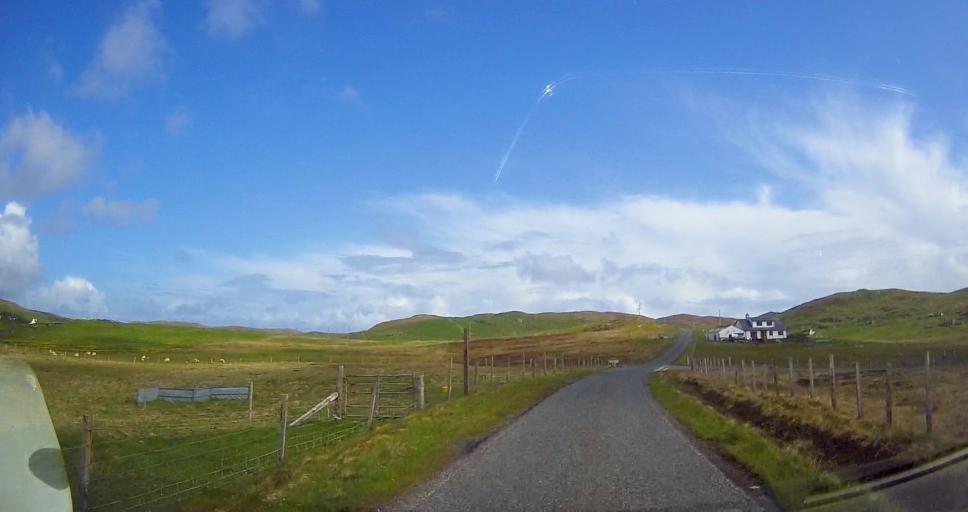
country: GB
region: Scotland
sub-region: Shetland Islands
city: Lerwick
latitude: 60.5905
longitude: -1.3356
